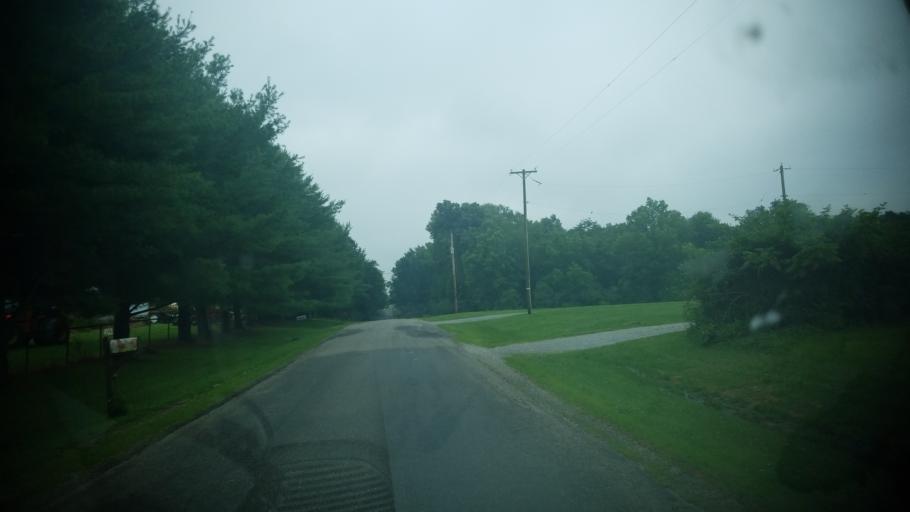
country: US
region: Illinois
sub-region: Clay County
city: Flora
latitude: 38.6700
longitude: -88.3548
